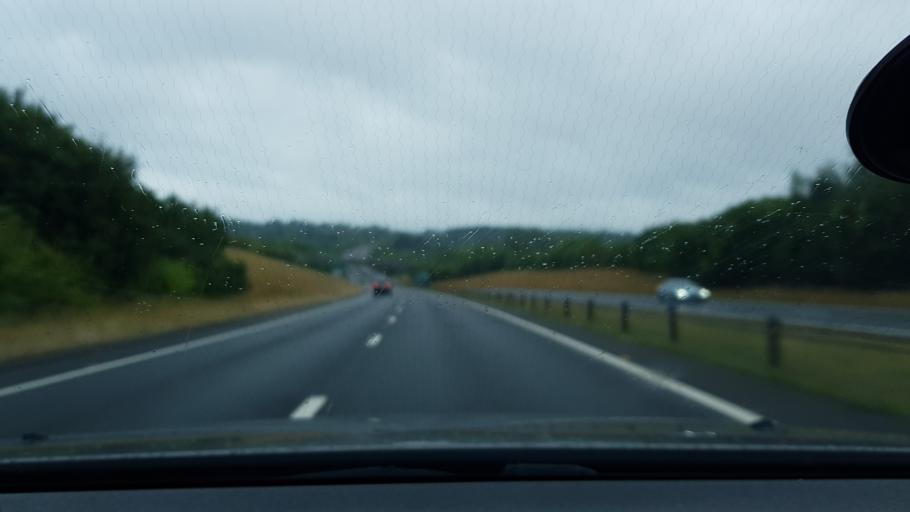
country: GB
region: England
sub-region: West Berkshire
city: Winterbourne
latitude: 51.4234
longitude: -1.3435
